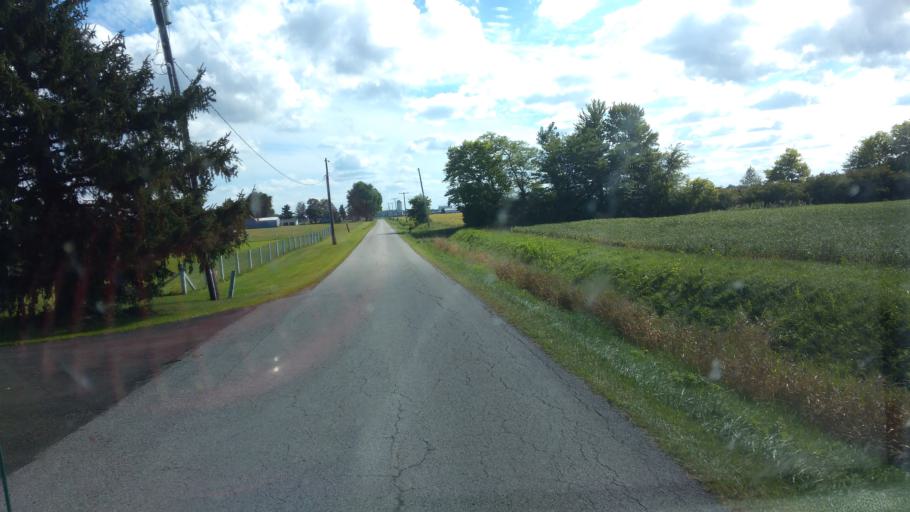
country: US
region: Ohio
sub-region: Sandusky County
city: Clyde
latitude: 41.3954
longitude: -82.9635
